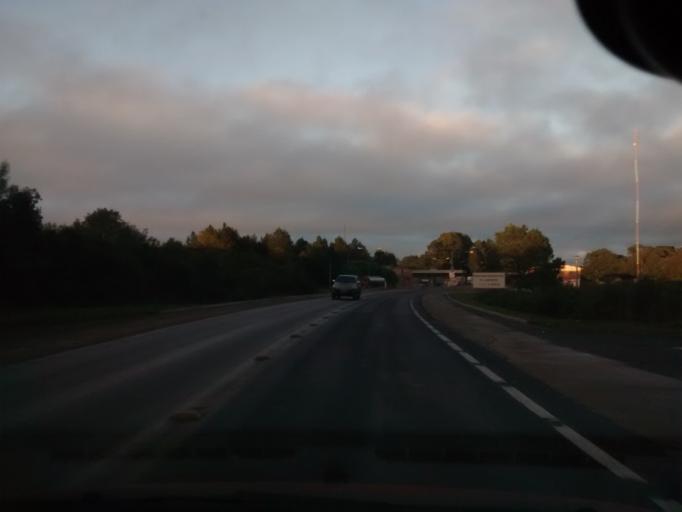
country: BR
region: Rio Grande do Sul
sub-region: Vacaria
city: Estrela
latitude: -28.2639
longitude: -50.7864
